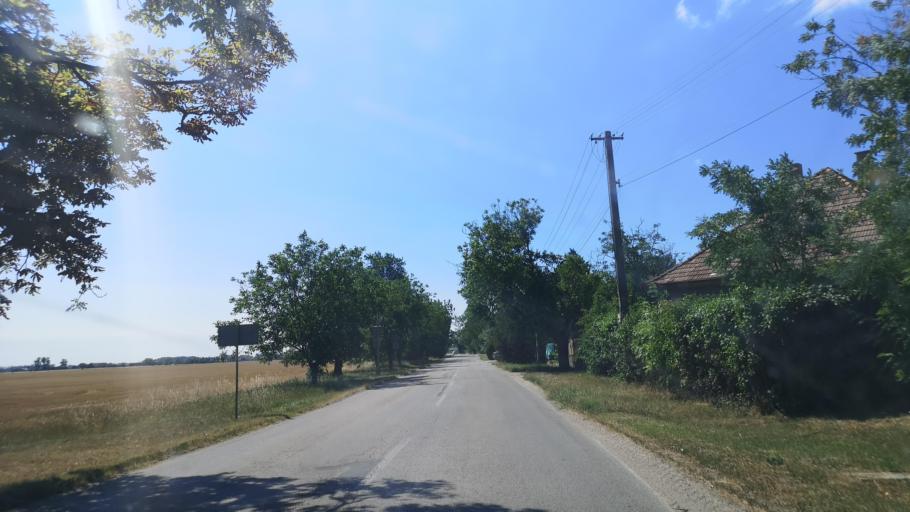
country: SK
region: Bratislavsky
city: Senec
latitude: 48.1115
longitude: 17.4712
